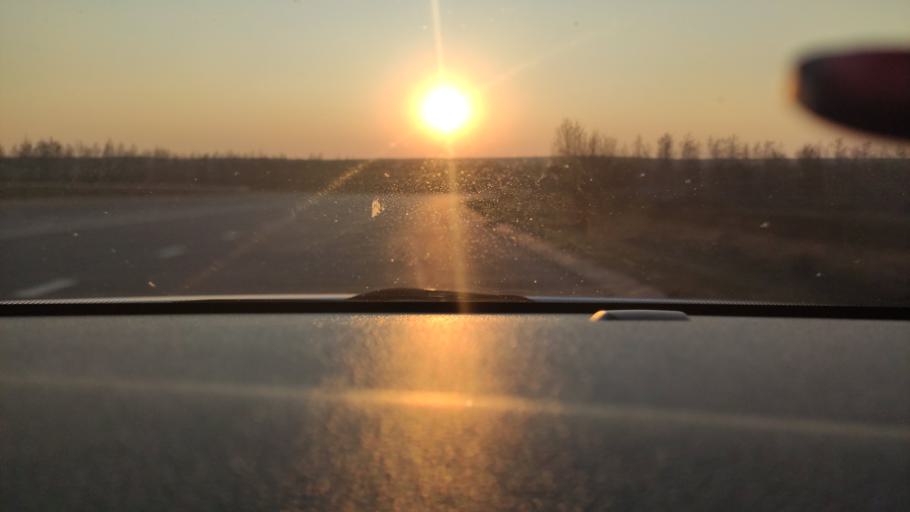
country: RU
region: Voronezj
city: Kolodeznyy
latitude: 51.3224
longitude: 39.1134
